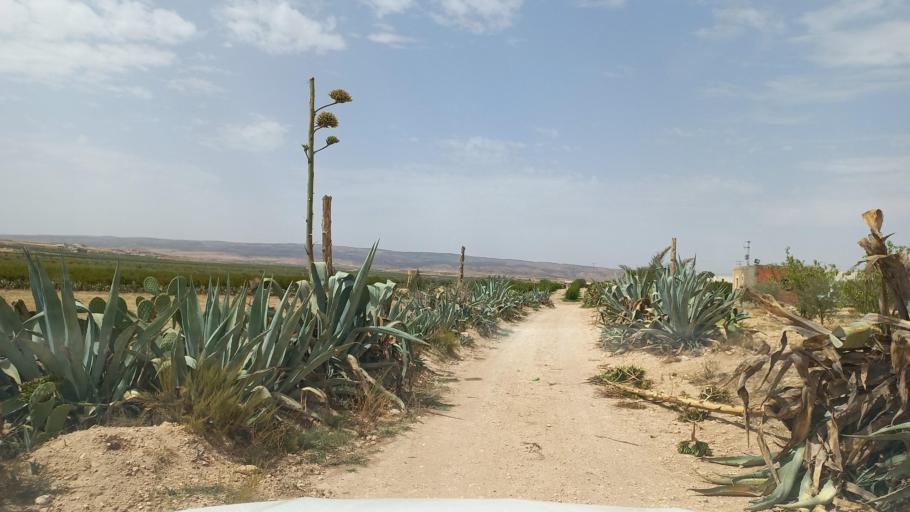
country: TN
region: Al Qasrayn
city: Kasserine
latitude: 35.2768
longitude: 9.0090
